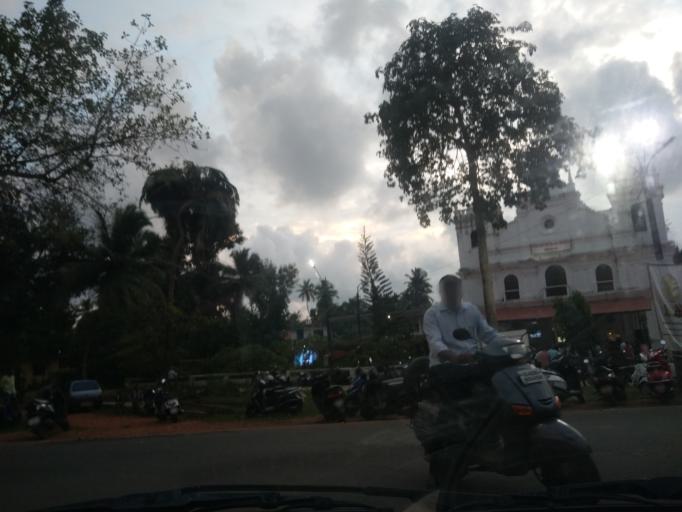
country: IN
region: Goa
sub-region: South Goa
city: Benaulim
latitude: 15.2892
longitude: 73.9412
